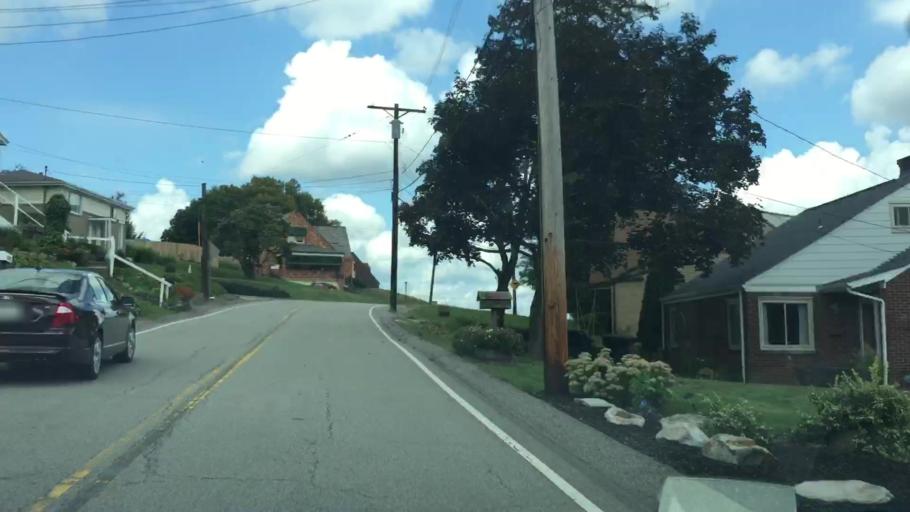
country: US
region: Pennsylvania
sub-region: Allegheny County
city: Millvale
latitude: 40.4998
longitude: -79.9995
